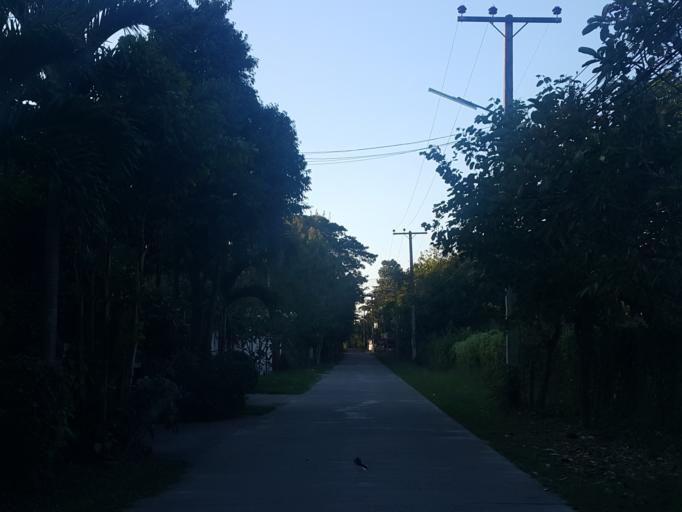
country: TH
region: Chiang Mai
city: San Sai
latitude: 18.8742
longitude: 99.1523
